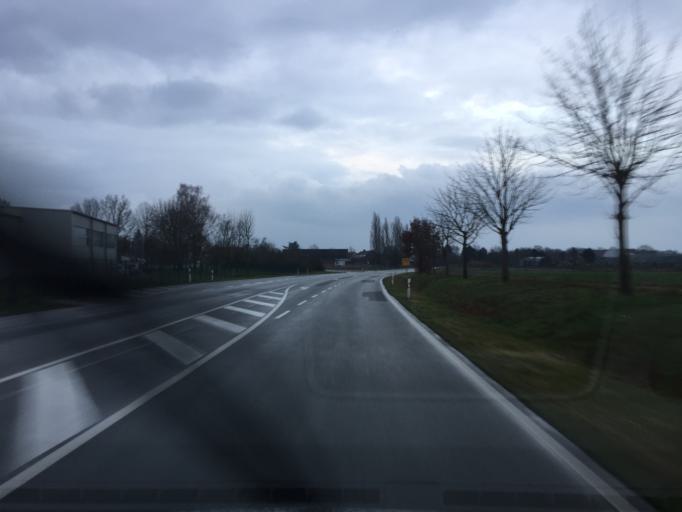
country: DE
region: Lower Saxony
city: Uchte
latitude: 52.5097
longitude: 8.9031
